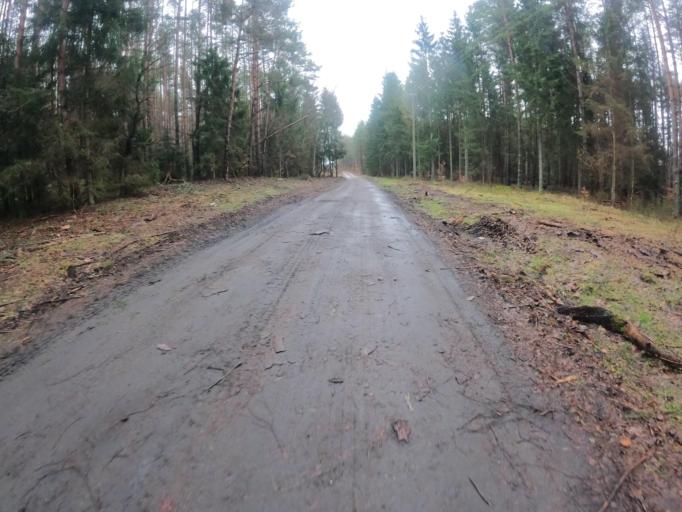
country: PL
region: West Pomeranian Voivodeship
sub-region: Powiat koszalinski
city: Polanow
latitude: 54.2246
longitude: 16.7206
